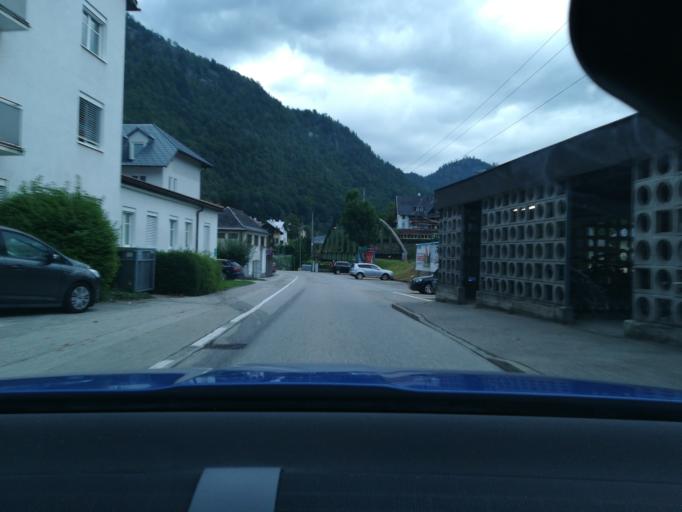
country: AT
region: Upper Austria
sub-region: Politischer Bezirk Gmunden
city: Bad Ischl
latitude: 47.7129
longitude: 13.6274
